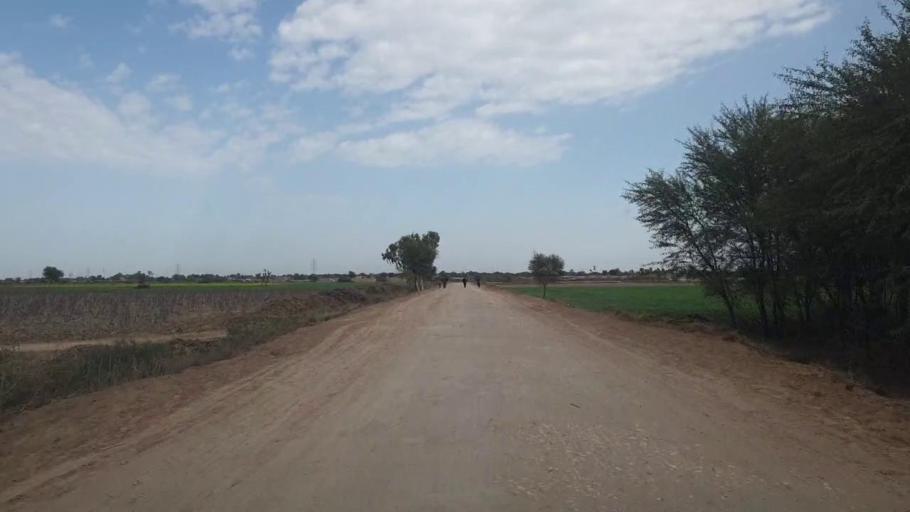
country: PK
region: Sindh
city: Sakrand
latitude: 26.0090
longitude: 68.3470
